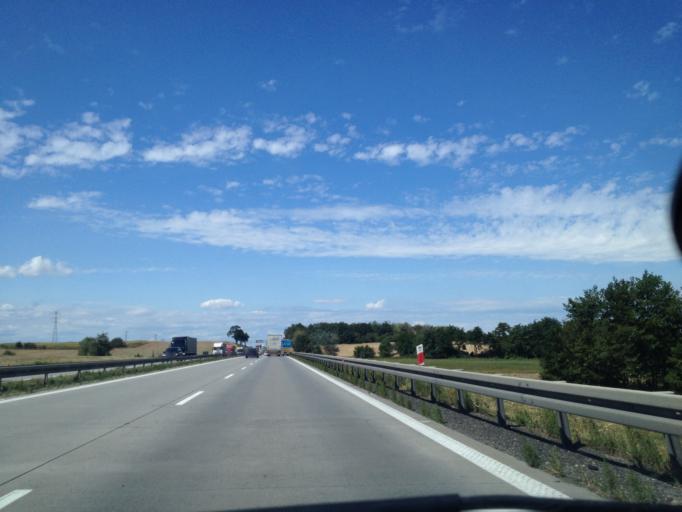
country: PL
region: Lower Silesian Voivodeship
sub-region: Powiat legnicki
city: Legnickie Pole
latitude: 51.1578
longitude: 16.2035
